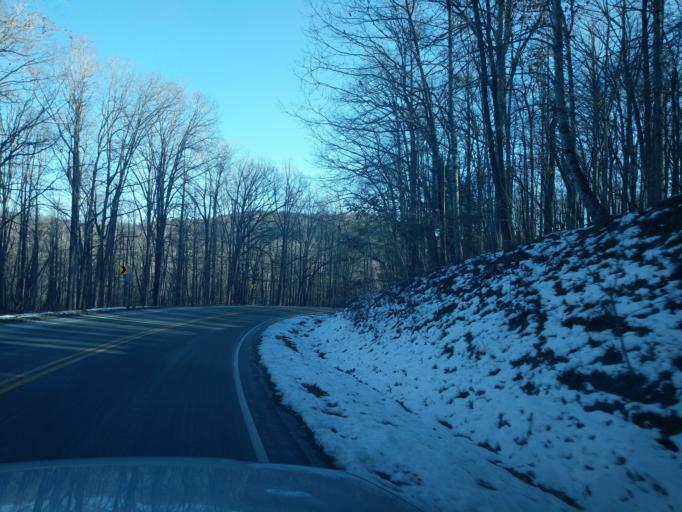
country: US
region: Georgia
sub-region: Rabun County
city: Clayton
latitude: 34.8754
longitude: -83.5690
